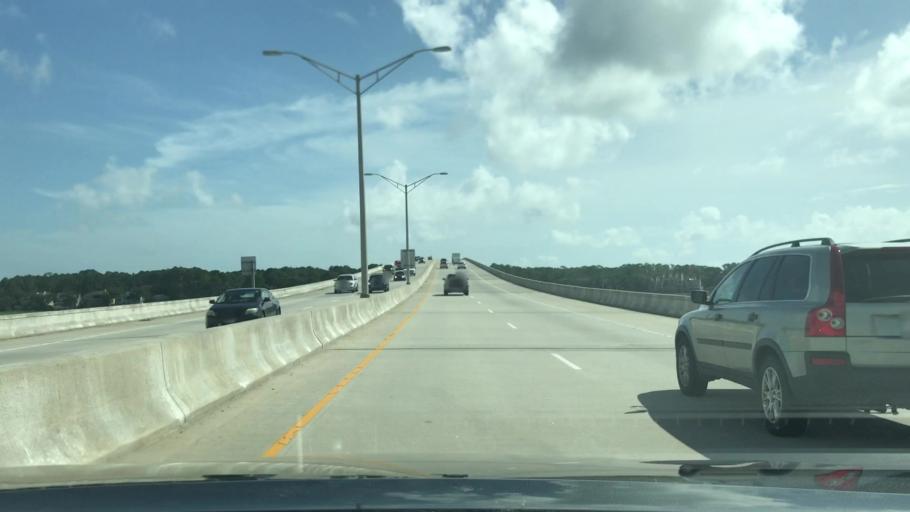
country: US
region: South Carolina
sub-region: Beaufort County
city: Hilton Head Island
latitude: 32.1822
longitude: -80.7666
